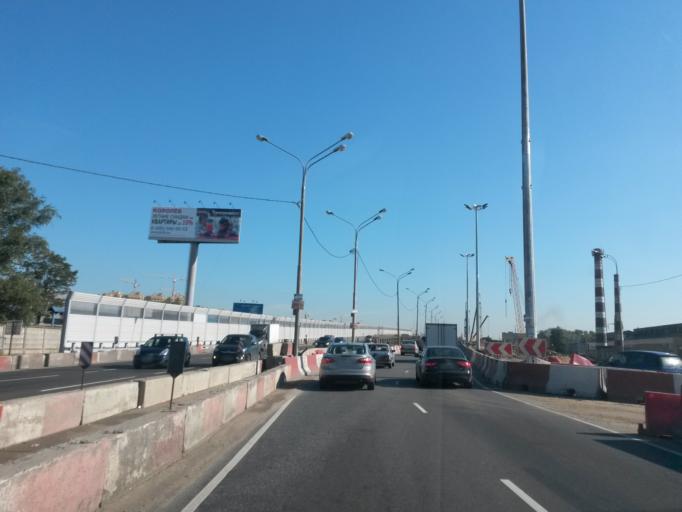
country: RU
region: Moskovskaya
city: Korolev
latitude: 55.9221
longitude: 37.7971
